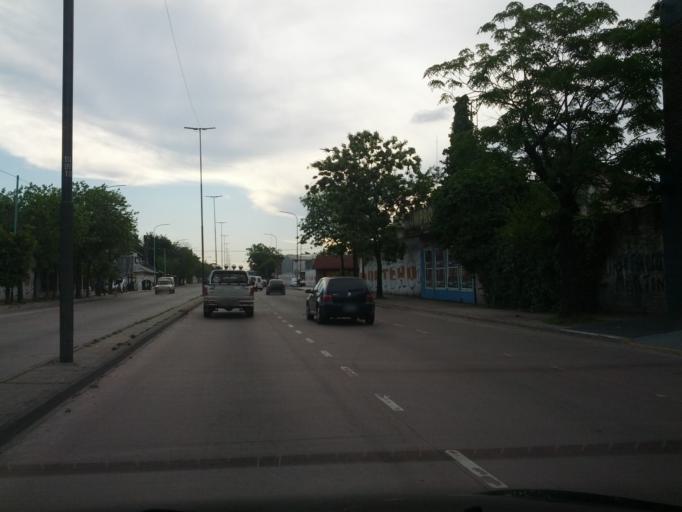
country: AR
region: Buenos Aires
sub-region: Partido de Avellaneda
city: Avellaneda
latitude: -34.6499
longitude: -58.4214
